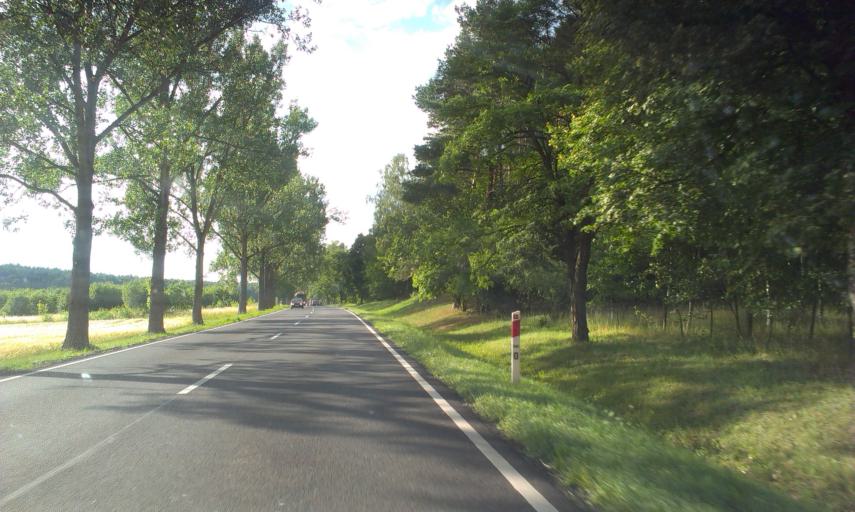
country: PL
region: Greater Poland Voivodeship
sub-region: Powiat zlotowski
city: Okonek
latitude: 53.4891
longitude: 16.8663
